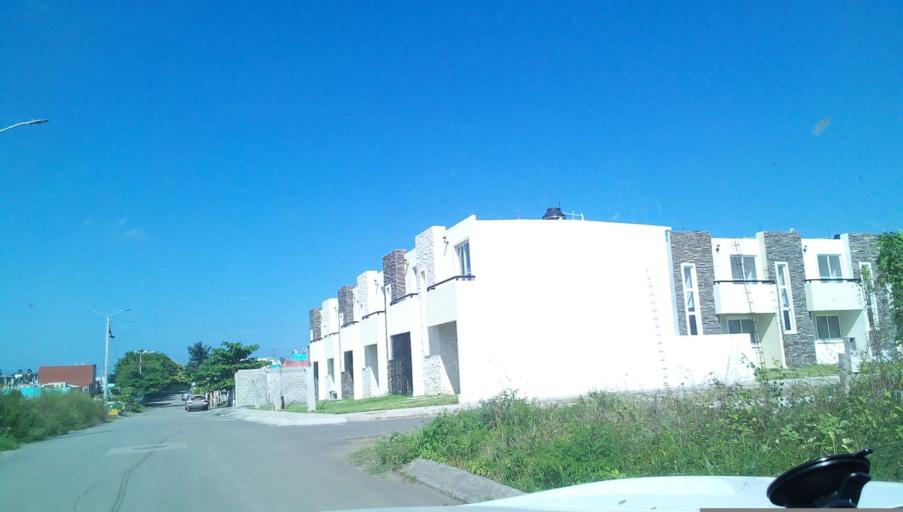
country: MX
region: Veracruz
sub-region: Veracruz
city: Las Amapolas
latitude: 19.1540
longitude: -96.2168
